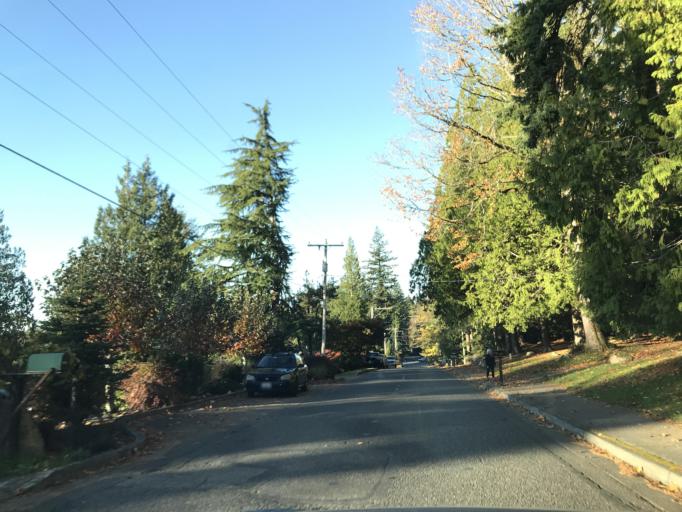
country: US
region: Washington
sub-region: Whatcom County
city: Geneva
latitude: 48.7463
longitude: -122.4263
